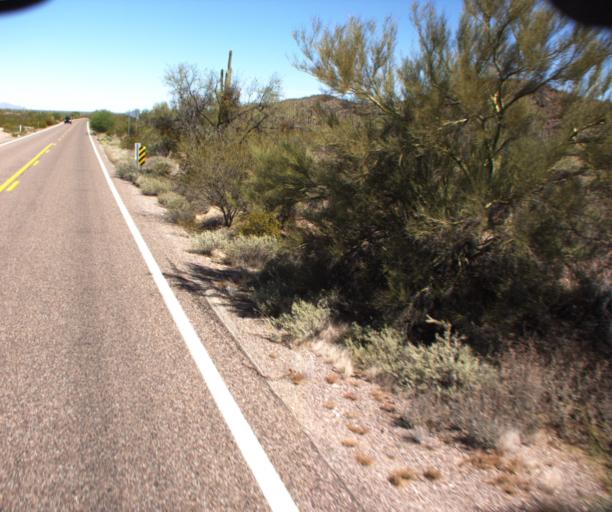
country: MX
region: Sonora
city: Sonoyta
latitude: 31.9975
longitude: -112.8063
